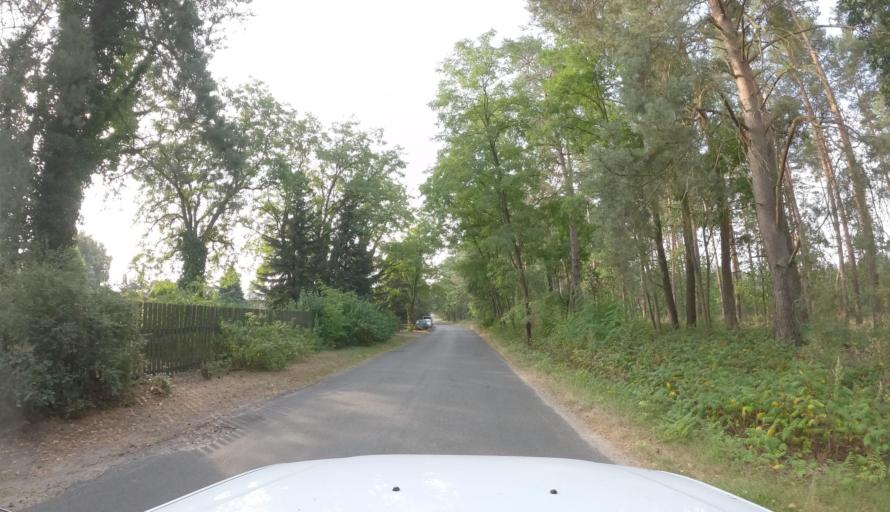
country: PL
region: West Pomeranian Voivodeship
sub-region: Powiat stargardzki
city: Kobylanka
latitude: 53.4317
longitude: 14.8974
